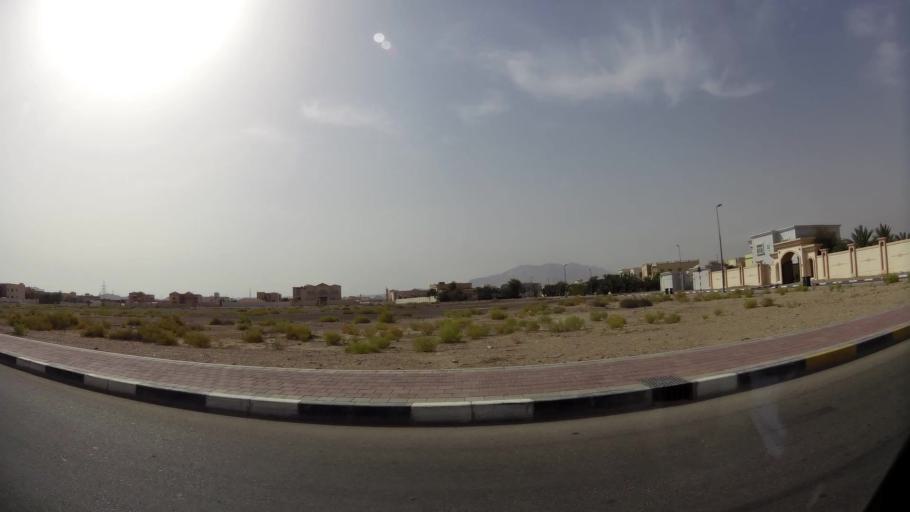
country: AE
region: Abu Dhabi
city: Al Ain
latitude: 24.1446
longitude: 55.7013
